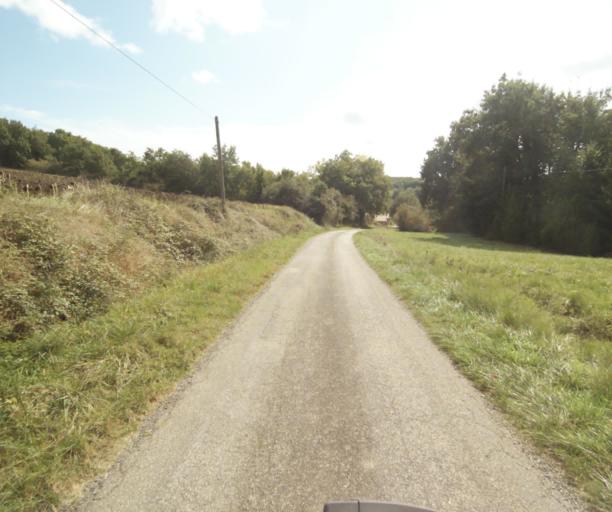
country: FR
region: Midi-Pyrenees
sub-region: Departement du Tarn-et-Garonne
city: Verdun-sur-Garonne
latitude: 43.8579
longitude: 1.1783
